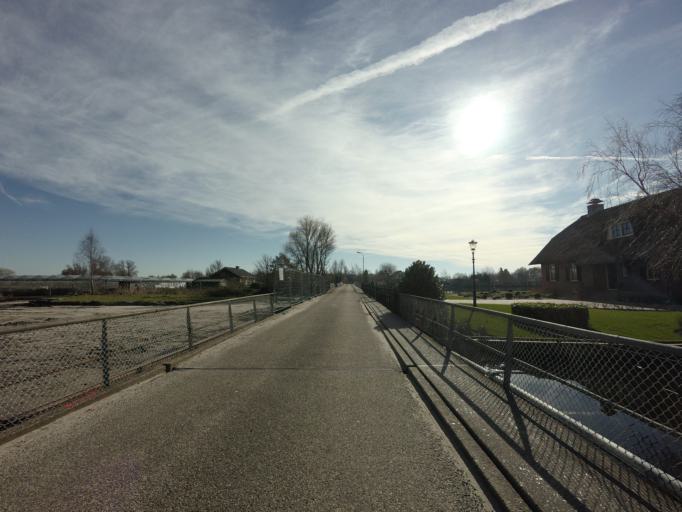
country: NL
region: South Holland
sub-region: Gemeente Kaag en Braassem
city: Oude Wetering
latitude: 52.2007
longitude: 4.6387
